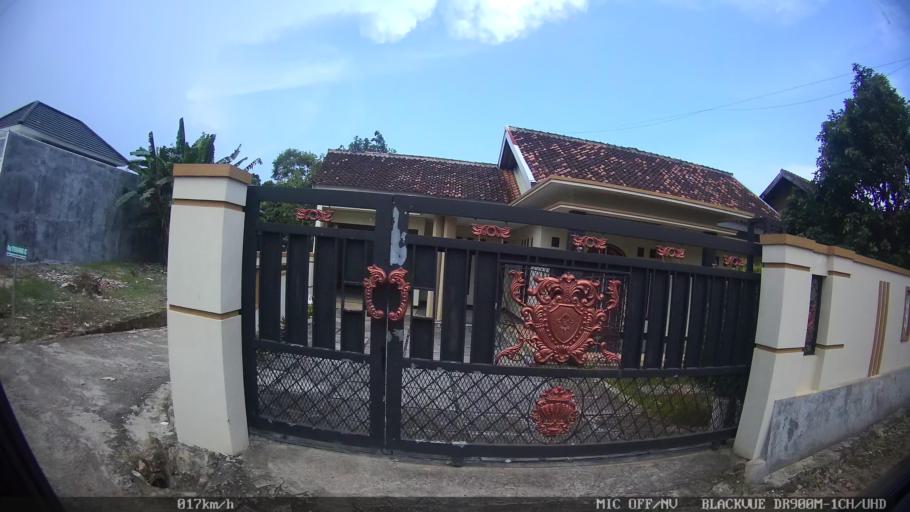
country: ID
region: Lampung
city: Kedaton
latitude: -5.3897
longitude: 105.2121
